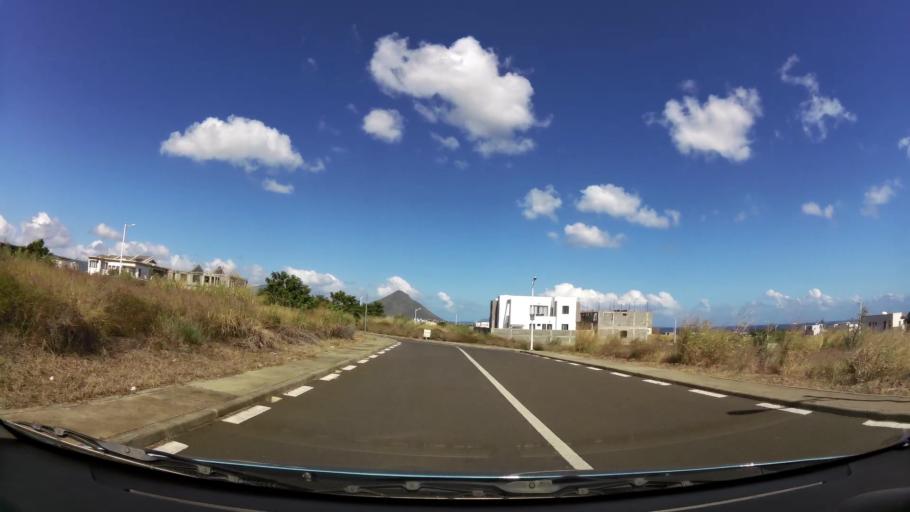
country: MU
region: Black River
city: Flic en Flac
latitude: -20.2779
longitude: 57.3829
